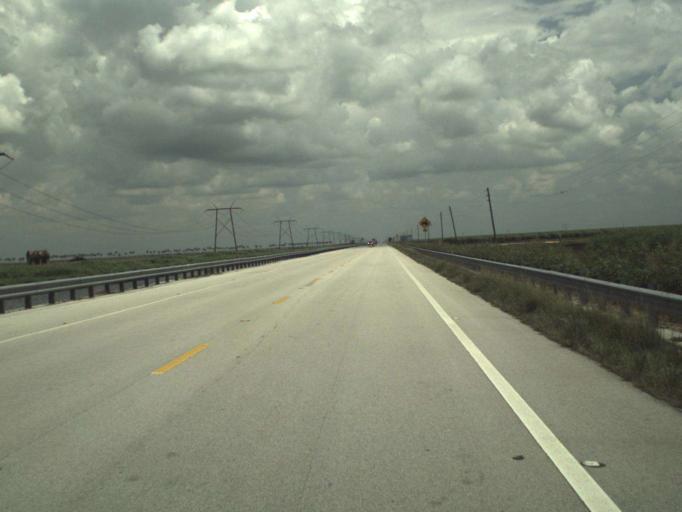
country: US
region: Florida
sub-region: Palm Beach County
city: Pahokee
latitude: 26.8211
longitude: -80.5745
